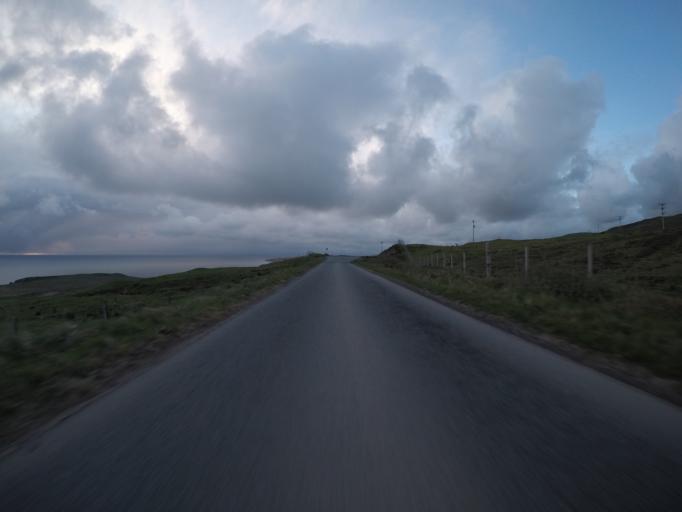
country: GB
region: Scotland
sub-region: Highland
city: Portree
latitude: 57.6012
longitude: -6.3774
